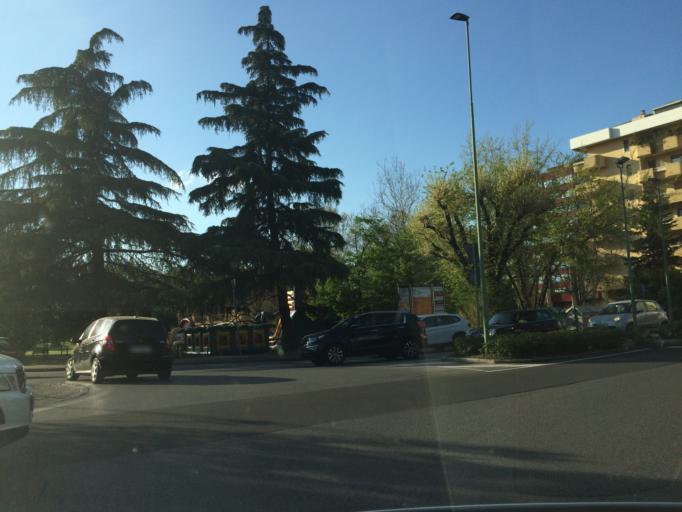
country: IT
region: Lombardy
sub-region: Provincia di Brescia
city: Brescia
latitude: 45.5263
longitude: 10.2112
